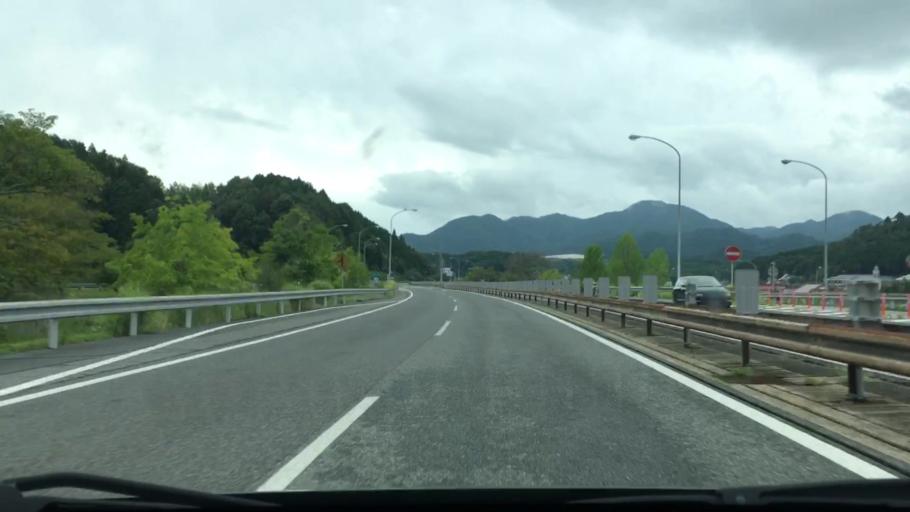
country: JP
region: Hiroshima
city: Hiroshima-shi
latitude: 34.6727
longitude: 132.5440
